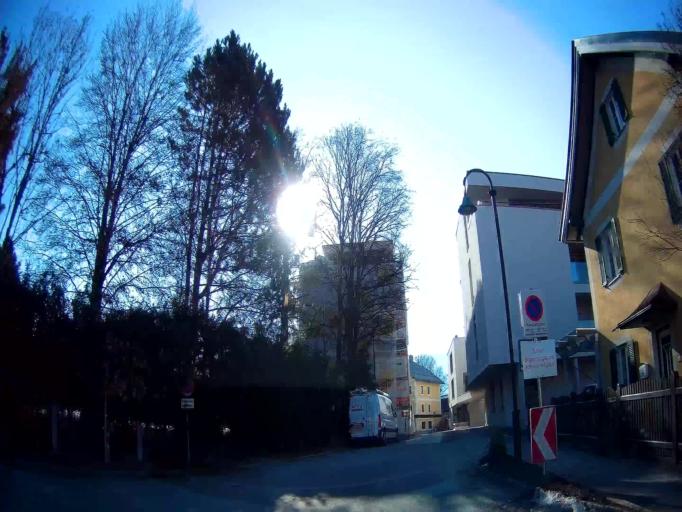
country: AT
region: Salzburg
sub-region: Politischer Bezirk Zell am See
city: Saalfelden am Steinernen Meer
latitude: 47.4283
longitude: 12.8470
